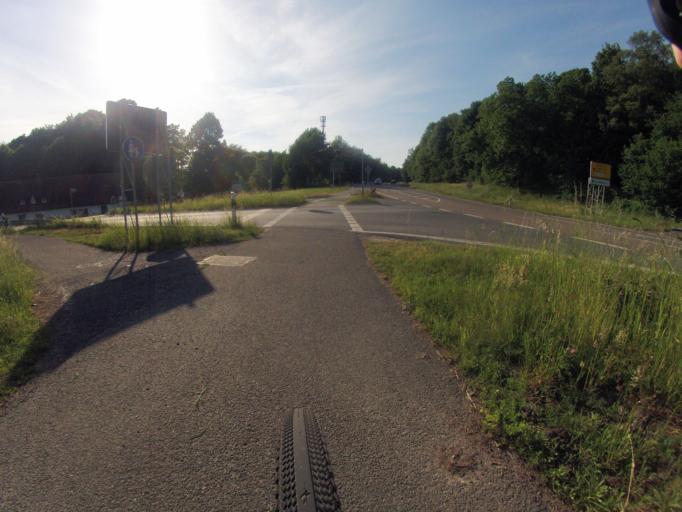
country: DE
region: North Rhine-Westphalia
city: Ibbenburen
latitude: 52.2955
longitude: 7.6982
